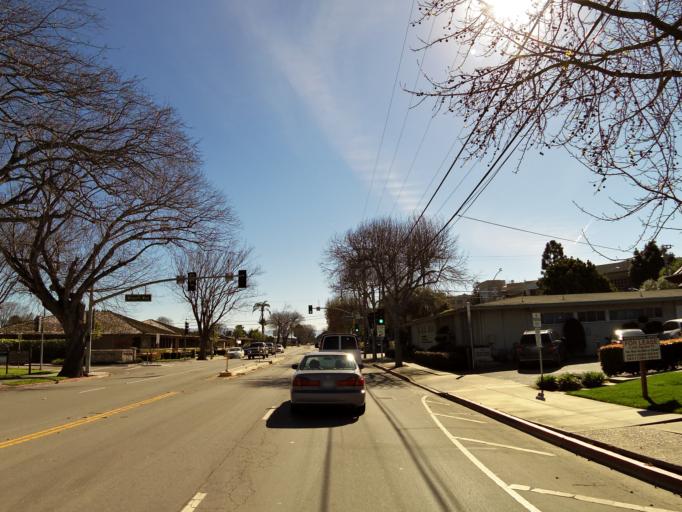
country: US
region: California
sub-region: Monterey County
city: Salinas
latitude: 36.6604
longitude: -121.6481
